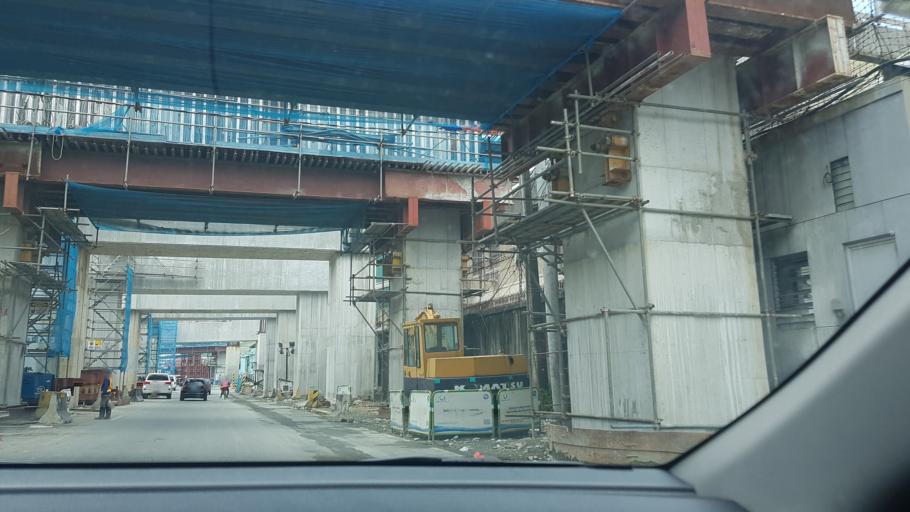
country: PH
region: Calabarzon
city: Del Monte
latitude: 14.6408
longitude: 121.0063
